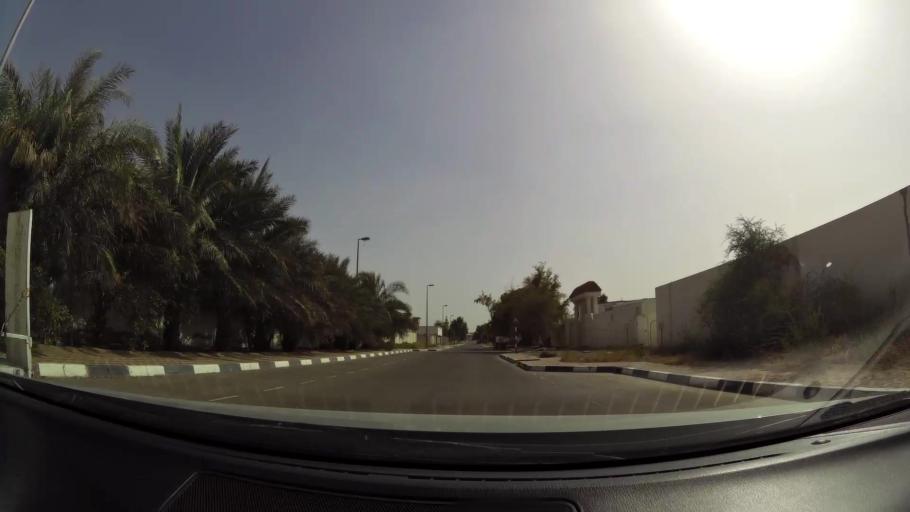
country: AE
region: Abu Dhabi
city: Al Ain
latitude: 24.2484
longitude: 55.6861
